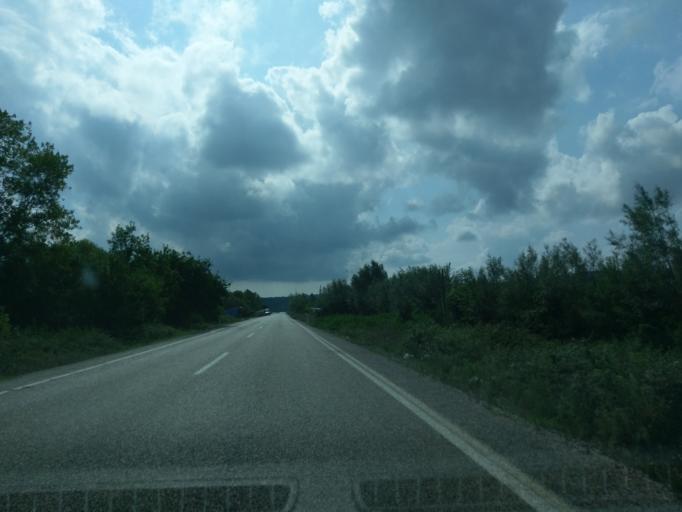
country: TR
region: Sinop
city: Sinop
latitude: 42.0166
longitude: 35.0529
